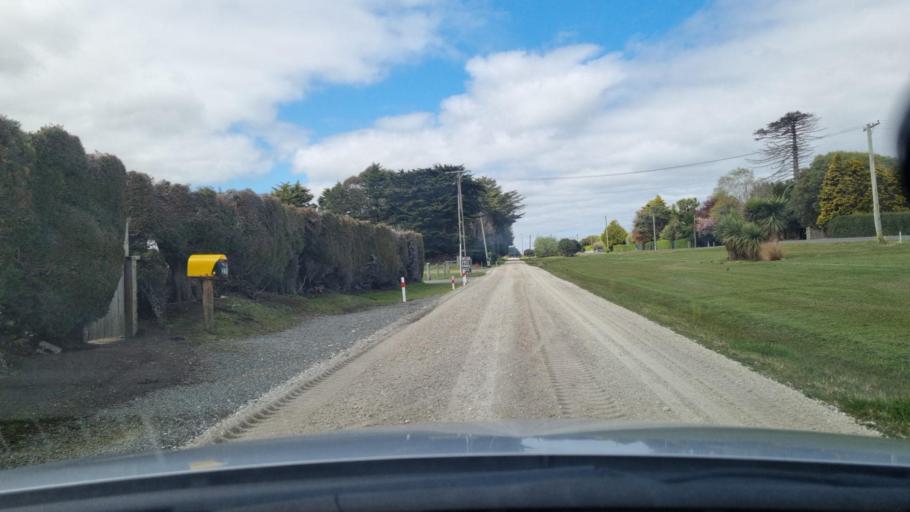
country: NZ
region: Southland
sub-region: Invercargill City
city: Invercargill
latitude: -46.4401
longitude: 168.3858
